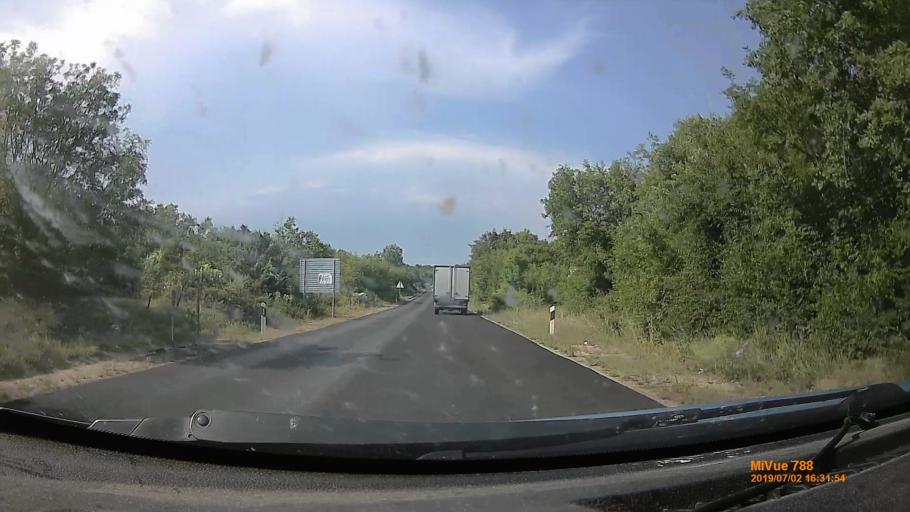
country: HR
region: Primorsko-Goranska
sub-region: Grad Krk
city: Krk
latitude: 45.0584
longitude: 14.4875
